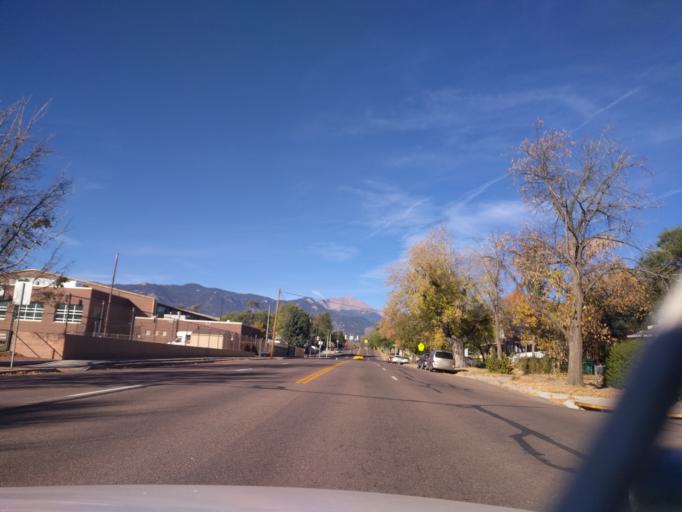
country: US
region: Colorado
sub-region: El Paso County
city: Colorado Springs
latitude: 38.8393
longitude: -104.8160
